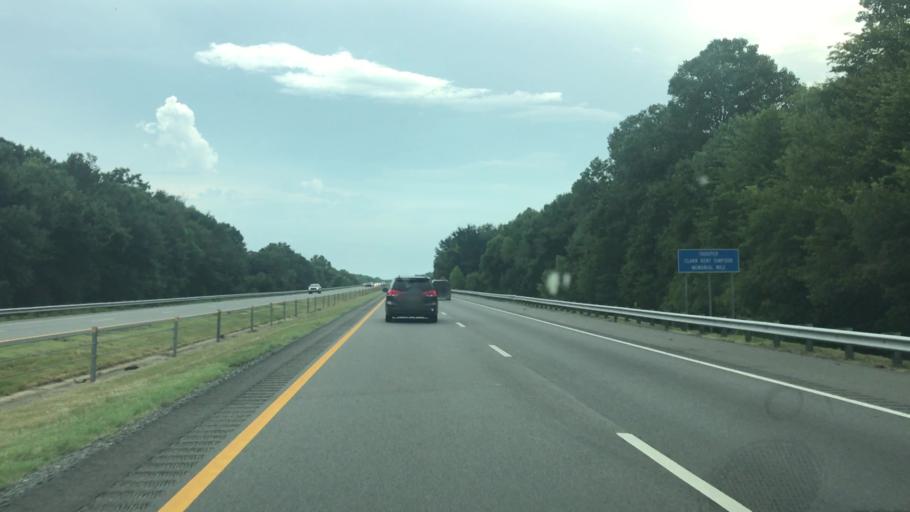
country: US
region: Arkansas
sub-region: Monroe County
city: Brinkley
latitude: 34.8885
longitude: -91.2552
